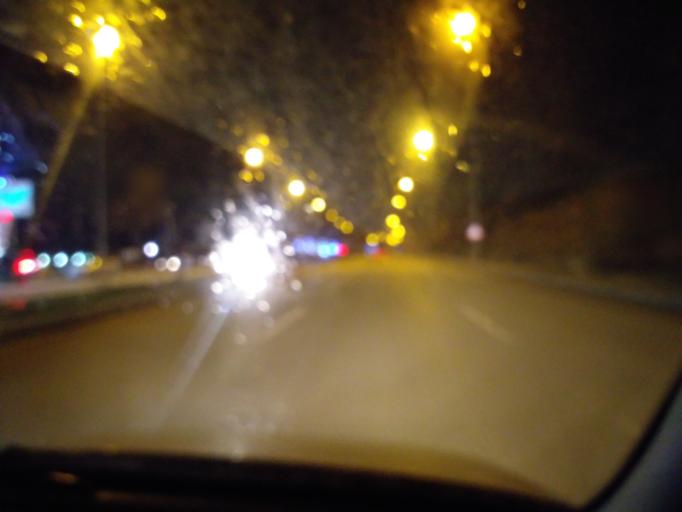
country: TR
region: Ankara
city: Batikent
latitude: 39.8838
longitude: 32.7141
